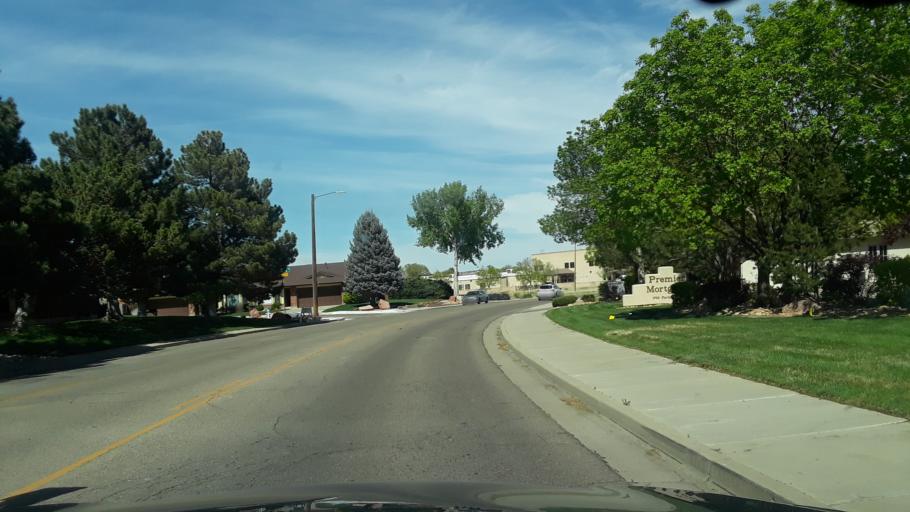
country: US
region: Colorado
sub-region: Pueblo County
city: Pueblo
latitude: 38.3119
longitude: -104.6296
